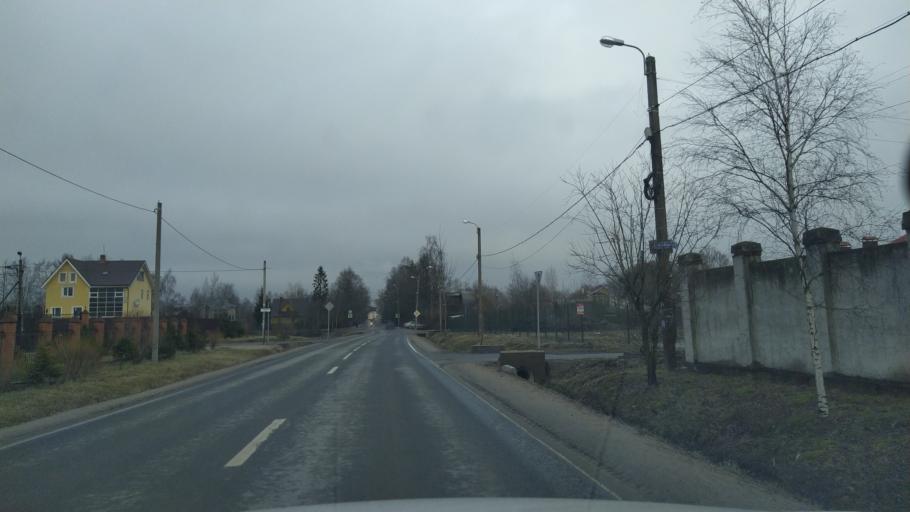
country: RU
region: St.-Petersburg
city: Aleksandrovskaya
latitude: 59.7250
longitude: 30.3503
